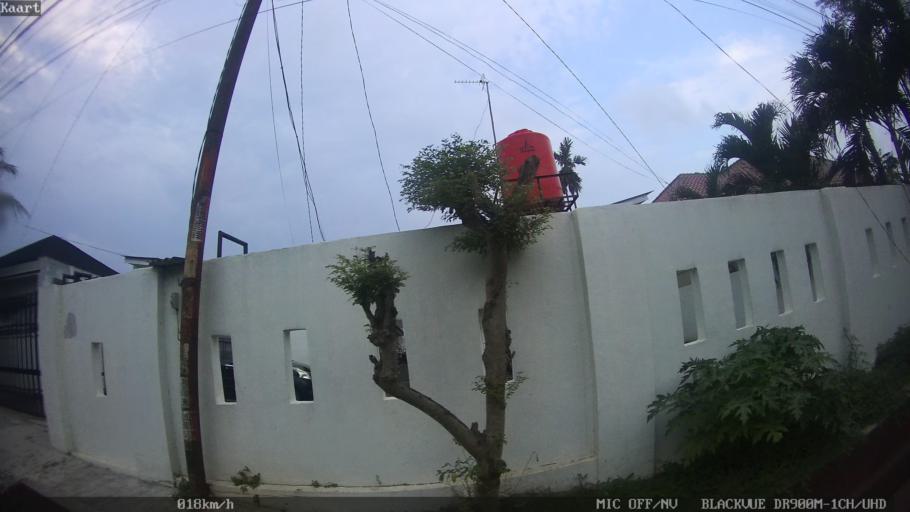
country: ID
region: Lampung
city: Kedaton
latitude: -5.4049
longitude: 105.2861
